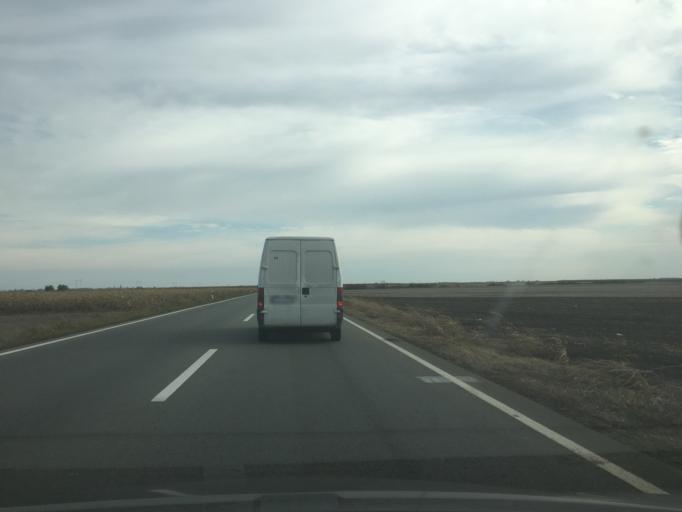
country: RS
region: Autonomna Pokrajina Vojvodina
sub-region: Juznobacki Okrug
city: Durdevo
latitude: 45.3403
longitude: 20.0067
